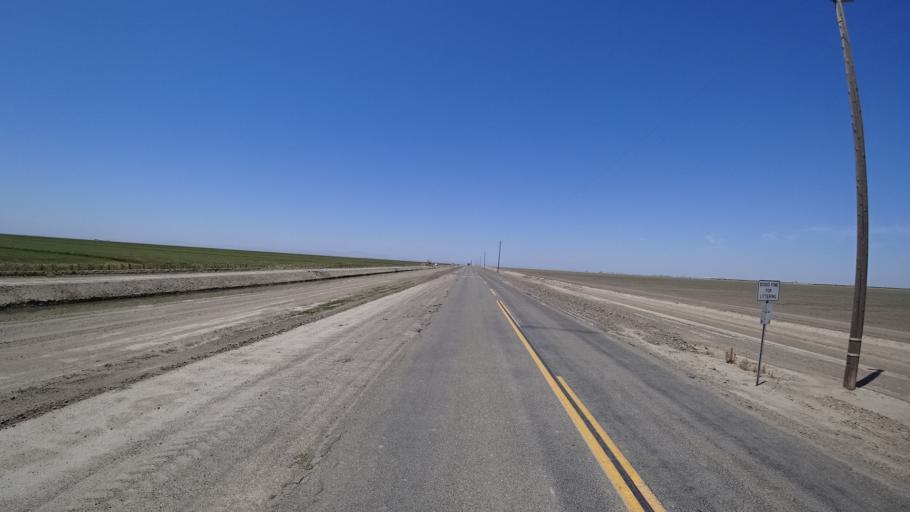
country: US
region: California
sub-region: Kings County
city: Corcoran
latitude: 36.1163
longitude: -119.6462
